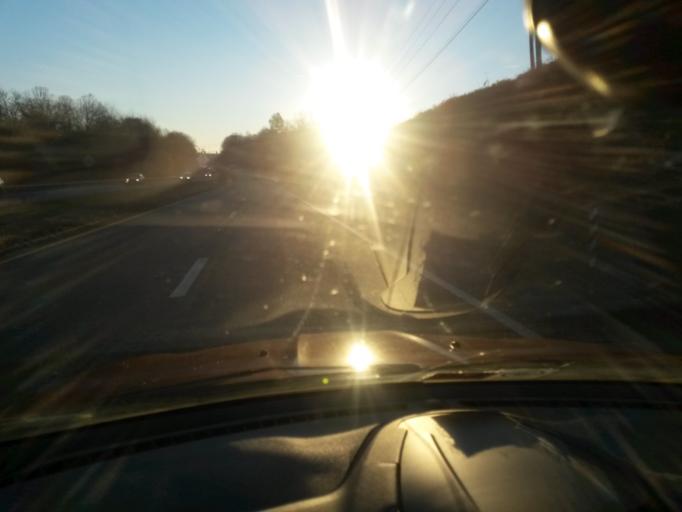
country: US
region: Virginia
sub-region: Franklin County
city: Rocky Mount
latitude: 37.0745
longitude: -79.9095
